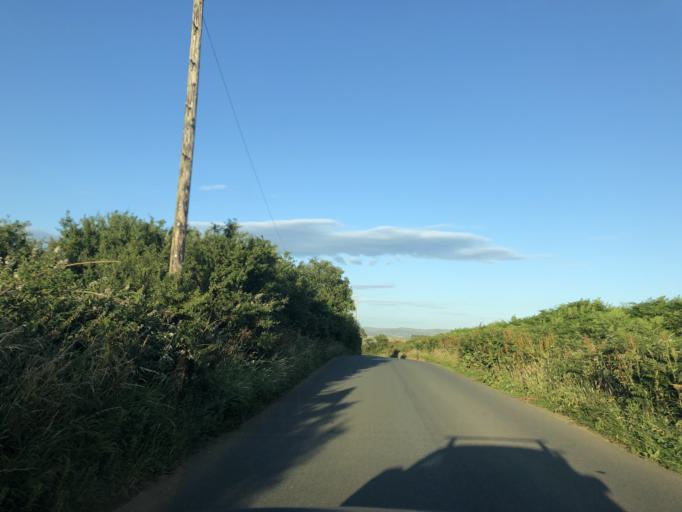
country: GB
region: England
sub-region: Isle of Wight
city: Chale
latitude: 50.6378
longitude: -1.3459
